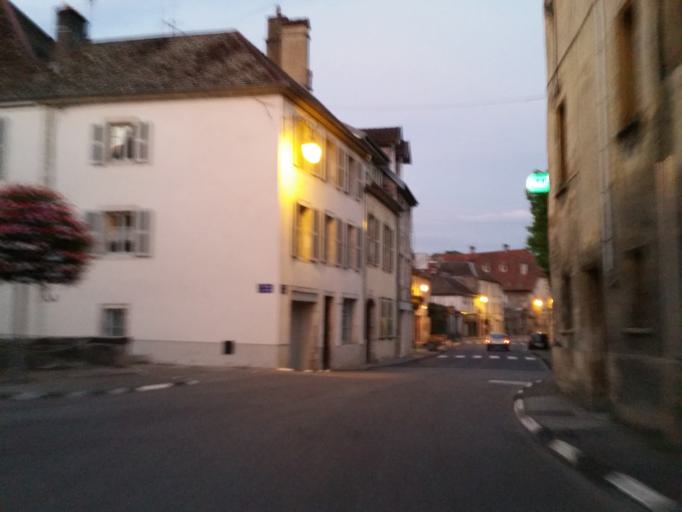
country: FR
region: Franche-Comte
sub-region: Departement du Doubs
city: Ornans
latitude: 47.1070
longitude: 6.1449
